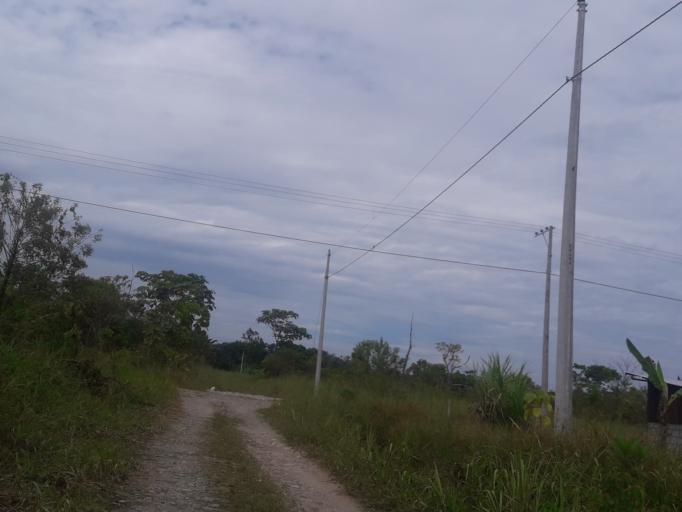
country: EC
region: Napo
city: Tena
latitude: -1.0581
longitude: -77.7946
